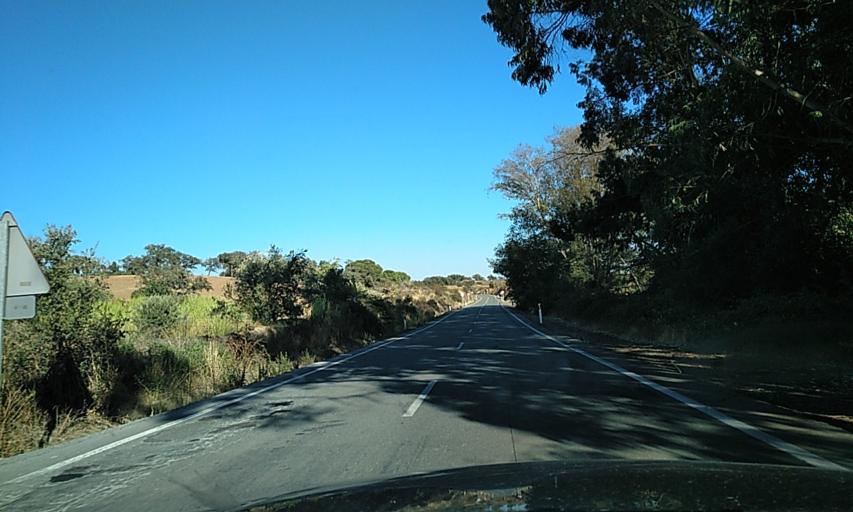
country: ES
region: Andalusia
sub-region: Provincia de Huelva
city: Santa Barbara de Casa
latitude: 37.7908
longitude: -7.1798
